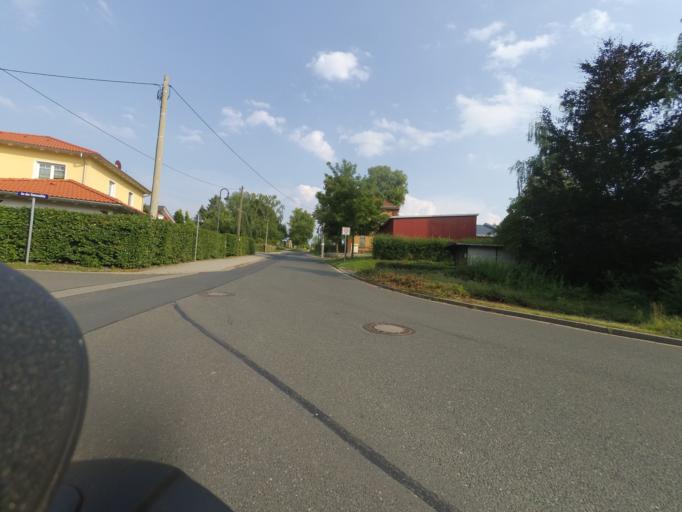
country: DE
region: Saxony
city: Wilsdruff
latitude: 51.0486
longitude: 13.5403
